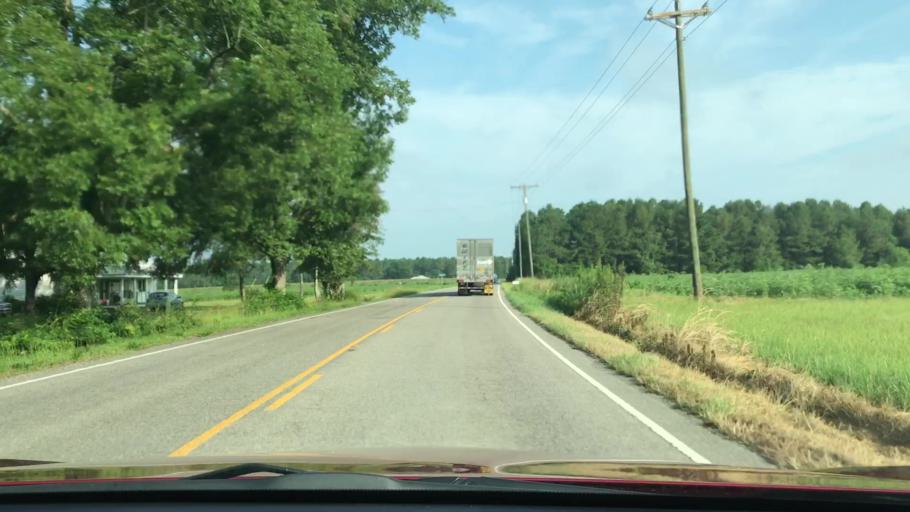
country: US
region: South Carolina
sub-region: Barnwell County
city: Blackville
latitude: 33.5972
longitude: -81.2584
